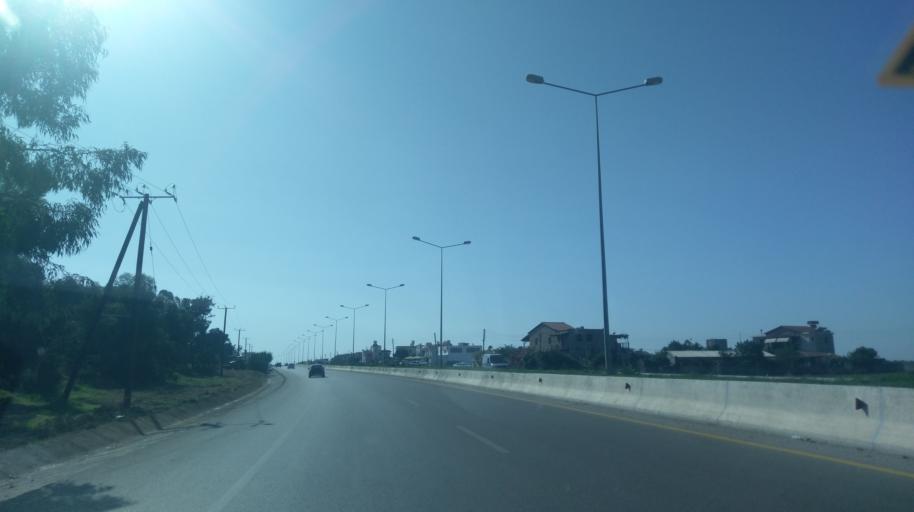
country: CY
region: Ammochostos
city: Trikomo
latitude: 35.2242
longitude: 33.8947
